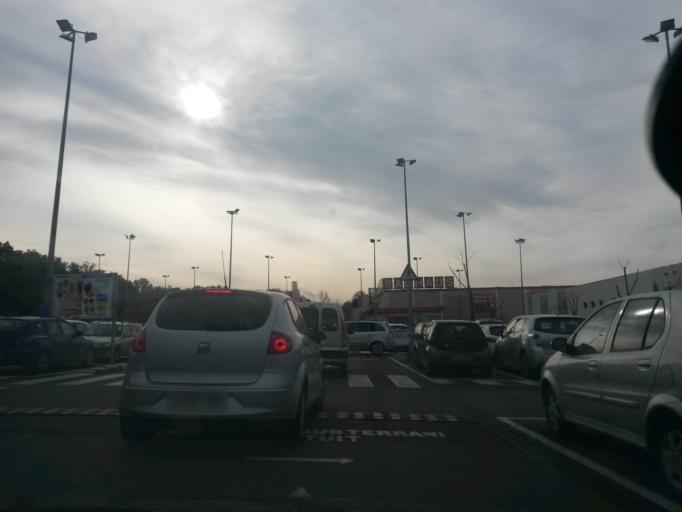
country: ES
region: Catalonia
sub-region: Provincia de Girona
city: Salt
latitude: 41.9604
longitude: 2.8120
